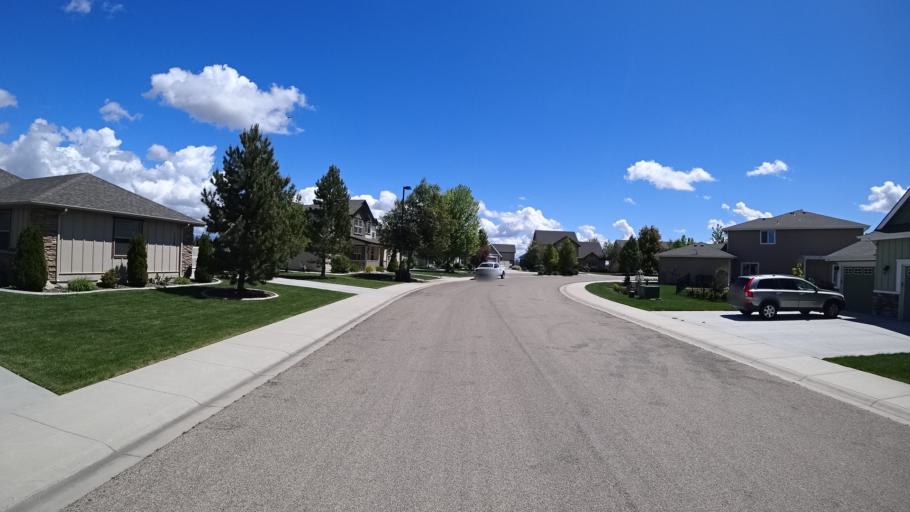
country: US
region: Idaho
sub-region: Ada County
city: Kuna
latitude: 43.5132
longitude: -116.4286
